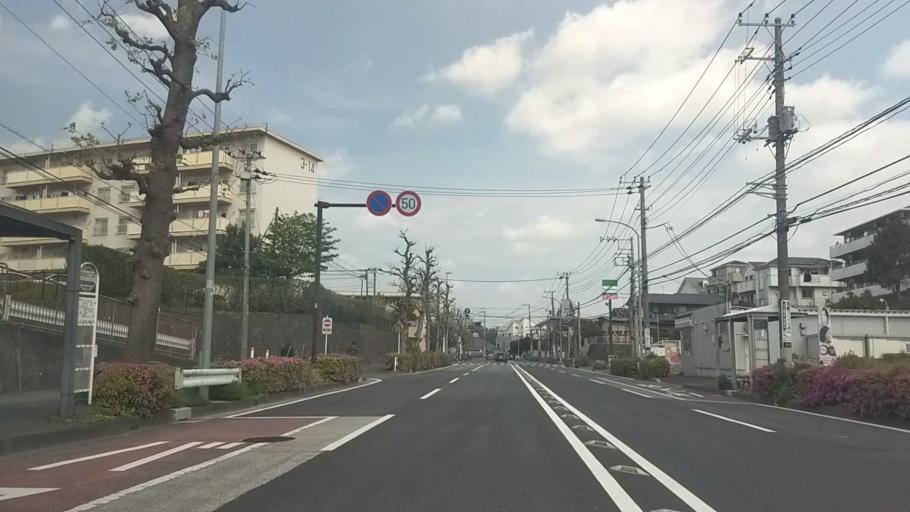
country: JP
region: Kanagawa
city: Yokohama
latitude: 35.3841
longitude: 139.5920
